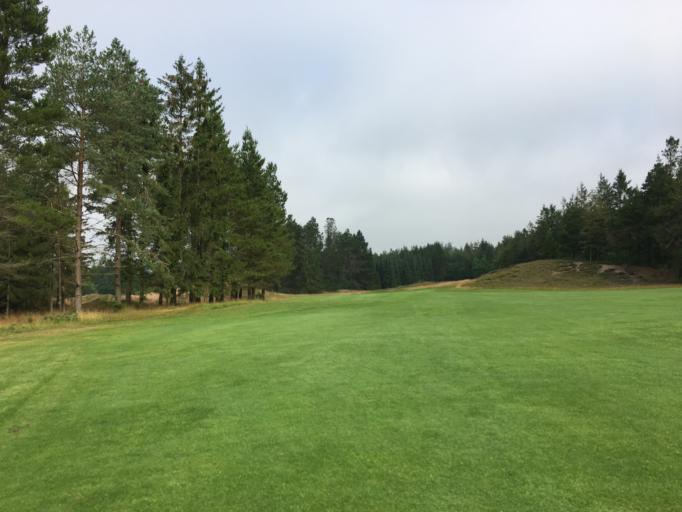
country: DK
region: Central Jutland
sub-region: Holstebro Kommune
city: Ulfborg
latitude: 56.3267
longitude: 8.4244
